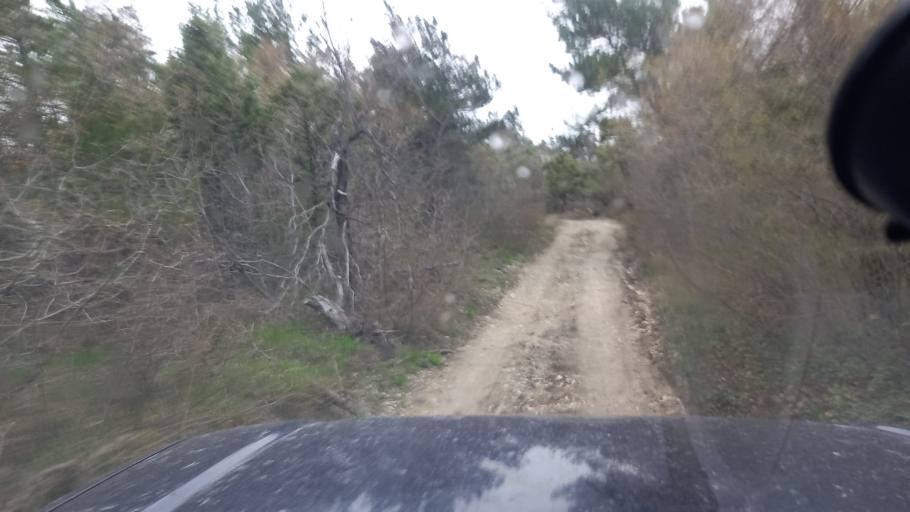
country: RU
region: Krasnodarskiy
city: Dzhubga
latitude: 44.3184
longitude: 38.6794
